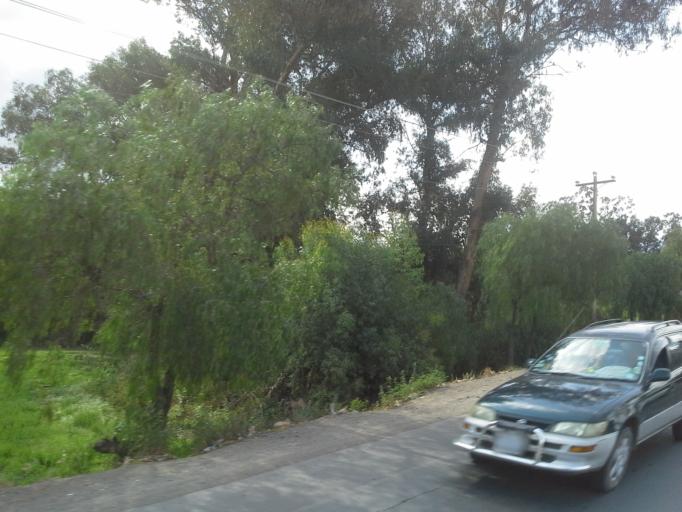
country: BO
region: Cochabamba
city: Cochabamba
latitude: -17.4935
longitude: -66.0928
